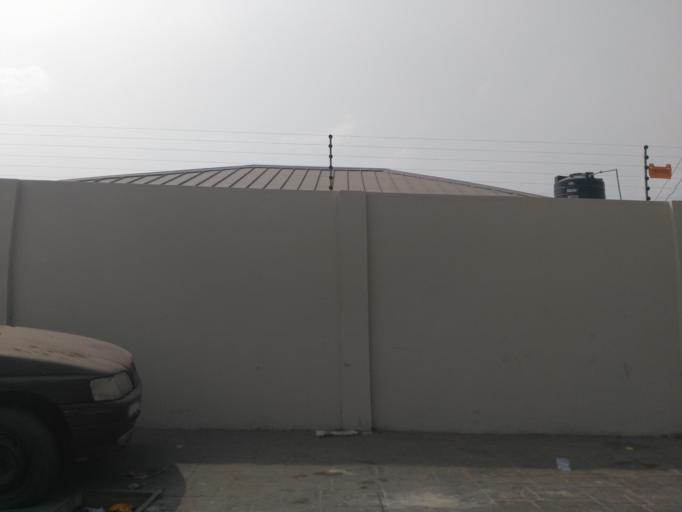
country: GH
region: Greater Accra
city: Accra
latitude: 5.5596
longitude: -0.1809
